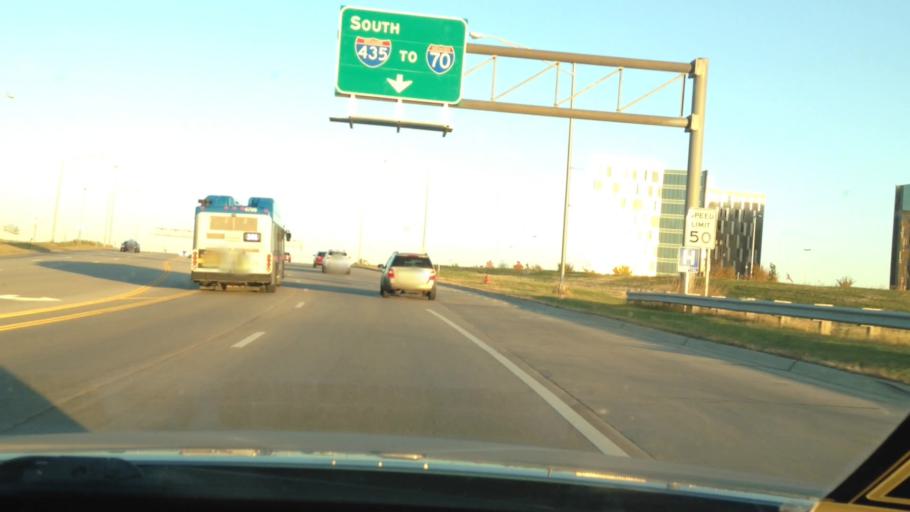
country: US
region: Kansas
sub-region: Wyandotte County
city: Edwardsville
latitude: 39.1163
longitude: -94.8181
